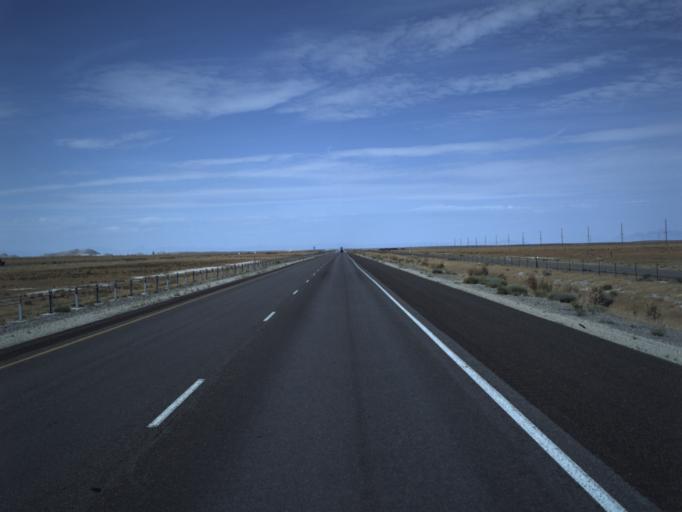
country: US
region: Utah
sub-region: Tooele County
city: Grantsville
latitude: 40.7265
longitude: -113.1825
